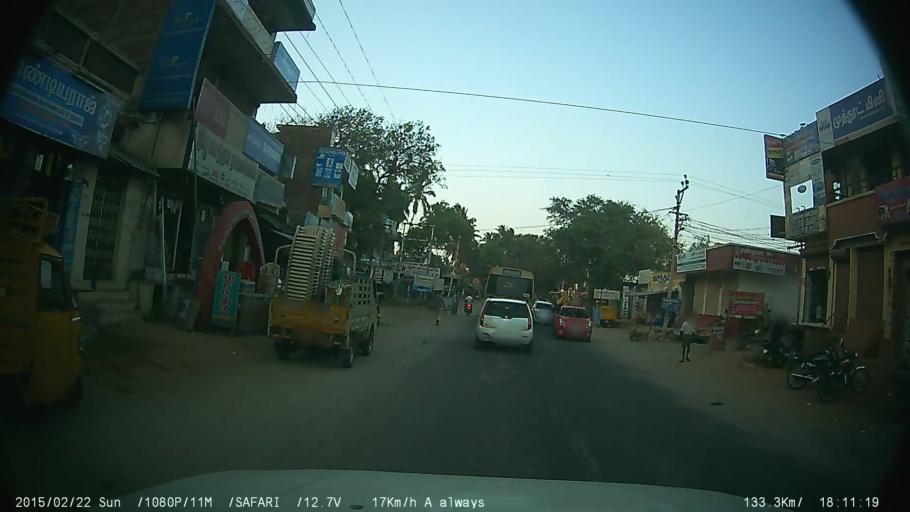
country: IN
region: Tamil Nadu
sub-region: Theni
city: Chinnamanur
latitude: 9.8435
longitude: 77.3802
